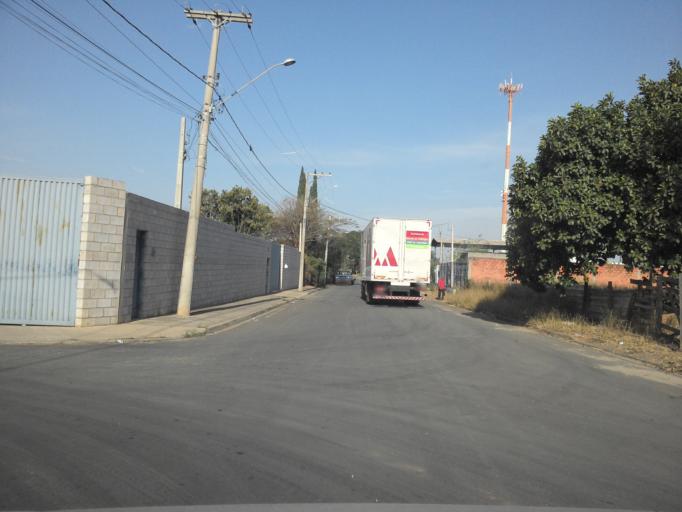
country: BR
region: Sao Paulo
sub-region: Hortolandia
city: Hortolandia
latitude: -22.9115
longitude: -47.2173
